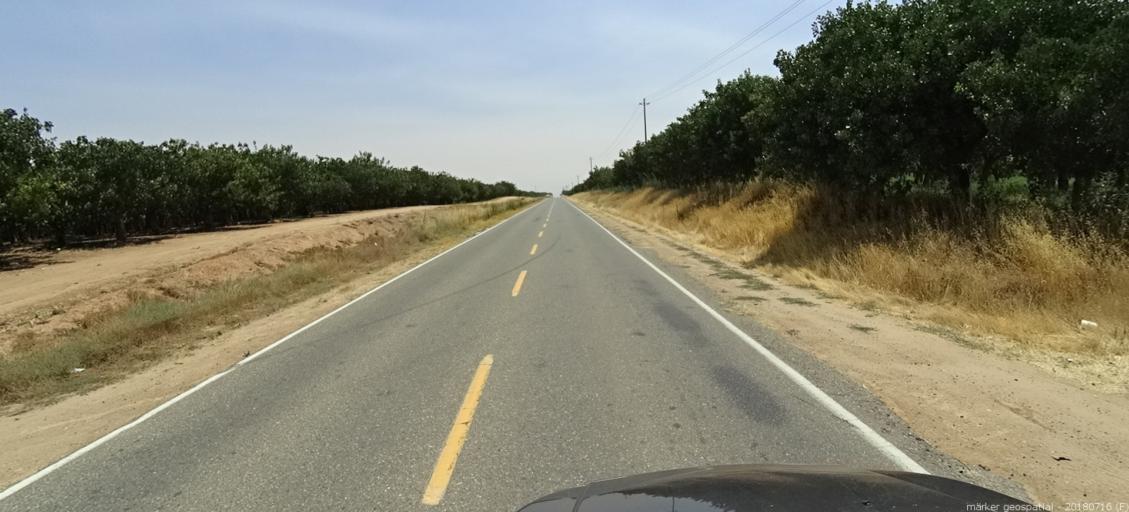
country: US
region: California
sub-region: Madera County
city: Madera Acres
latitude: 37.0544
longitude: -120.0689
